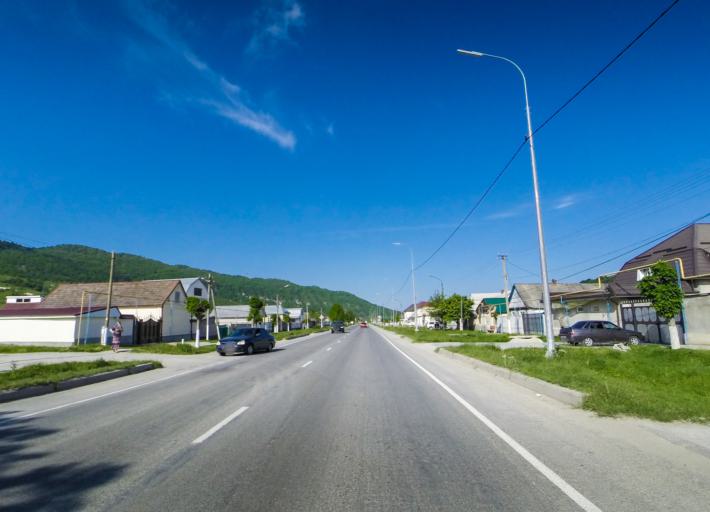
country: RU
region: Kabardino-Balkariya
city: Kashkhatau
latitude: 43.3214
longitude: 43.6169
